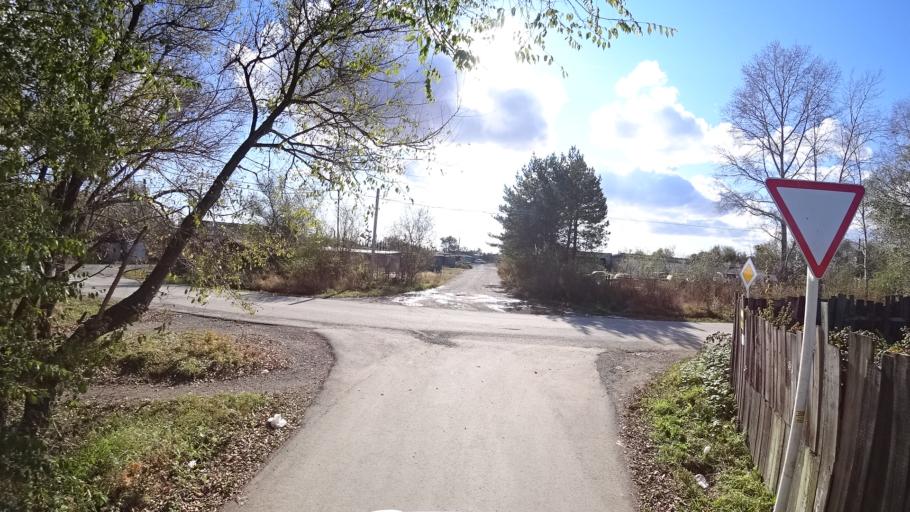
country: RU
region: Khabarovsk Krai
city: Amursk
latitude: 50.0992
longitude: 136.5037
